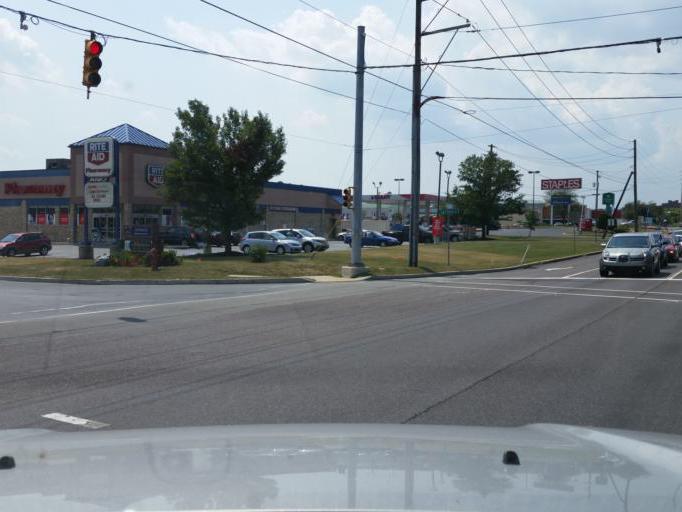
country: US
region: Pennsylvania
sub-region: Dauphin County
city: Progress
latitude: 40.2791
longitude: -76.8137
